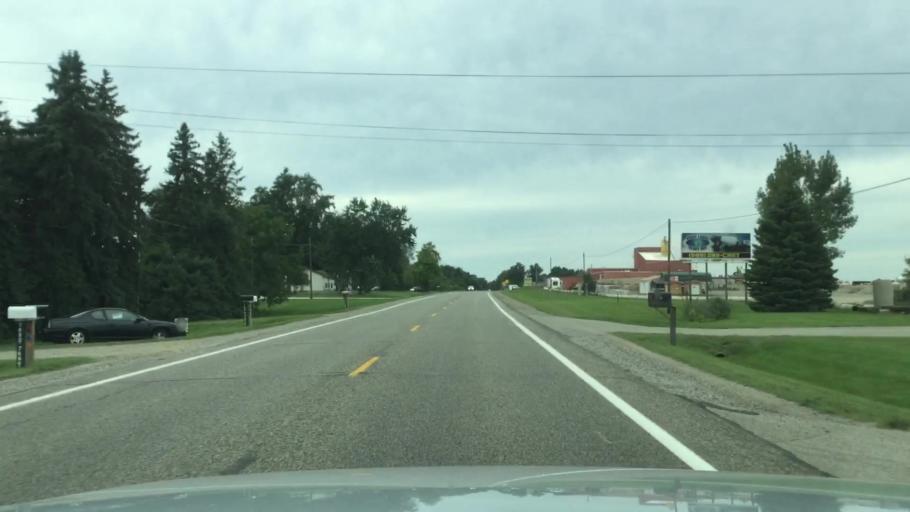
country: US
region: Michigan
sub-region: Shiawassee County
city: Durand
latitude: 42.9361
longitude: -84.0159
